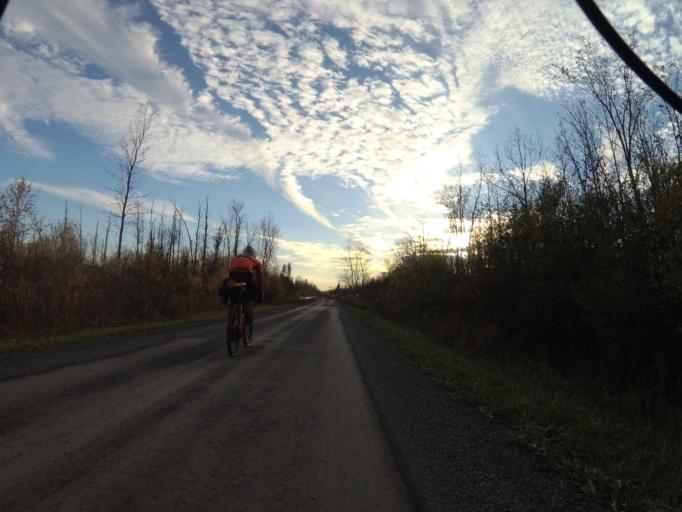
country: CA
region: Ontario
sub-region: Lanark County
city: Smiths Falls
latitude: 44.9856
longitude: -75.8021
